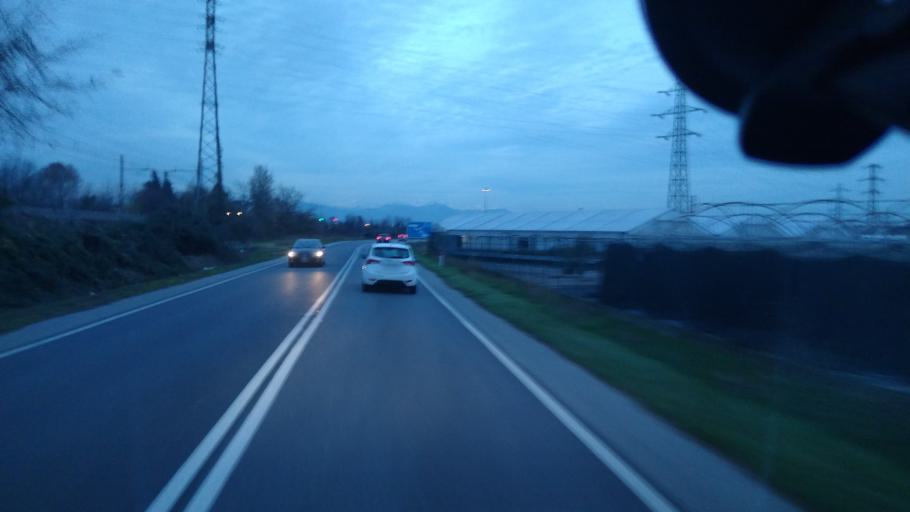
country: IT
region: Lombardy
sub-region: Provincia di Bergamo
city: Arcene
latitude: 45.5800
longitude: 9.6081
